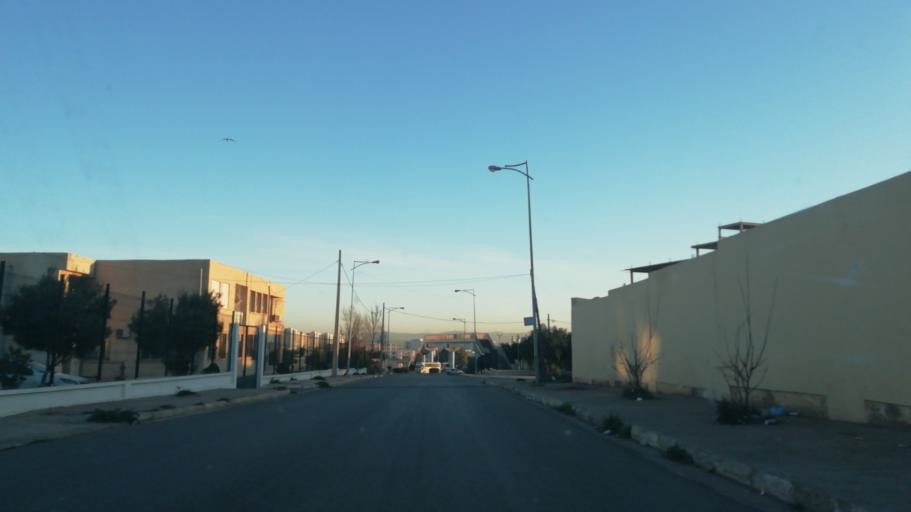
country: DZ
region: Oran
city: Bir el Djir
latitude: 35.7113
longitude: -0.5869
